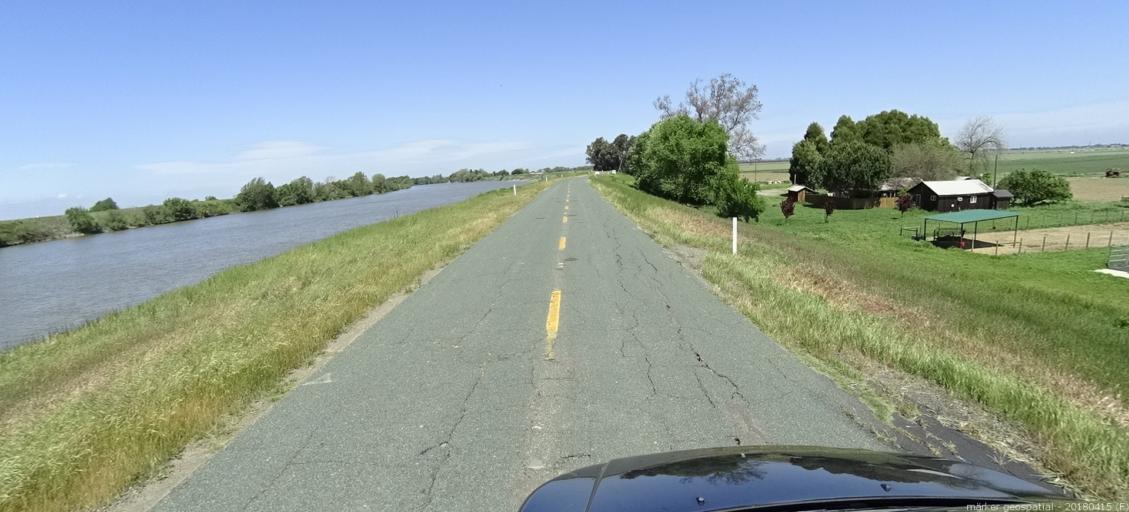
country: US
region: California
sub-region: Sacramento County
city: Walnut Grove
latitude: 38.2392
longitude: -121.6019
